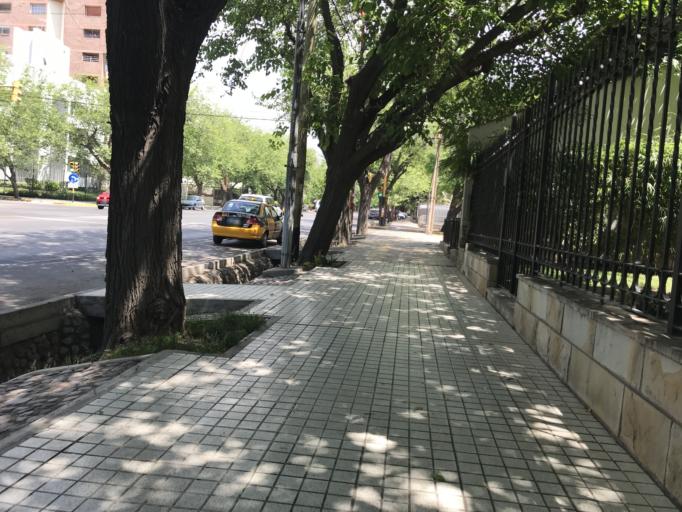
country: AR
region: Mendoza
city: Mendoza
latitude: -32.8874
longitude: -68.8563
